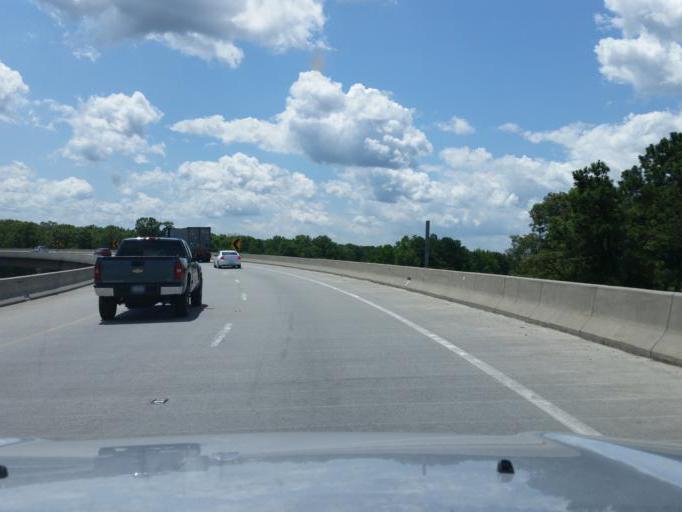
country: US
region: Virginia
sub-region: Henrico County
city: Sandston
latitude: 37.5199
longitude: -77.2715
